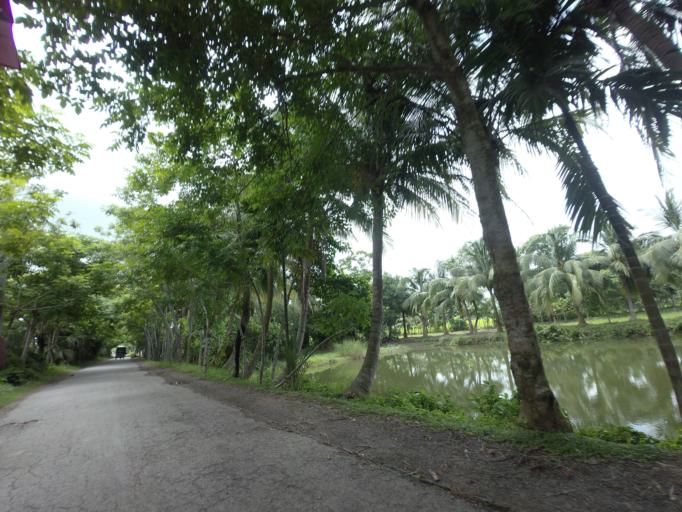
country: BD
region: Khulna
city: Kalia
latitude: 23.0399
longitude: 89.6394
